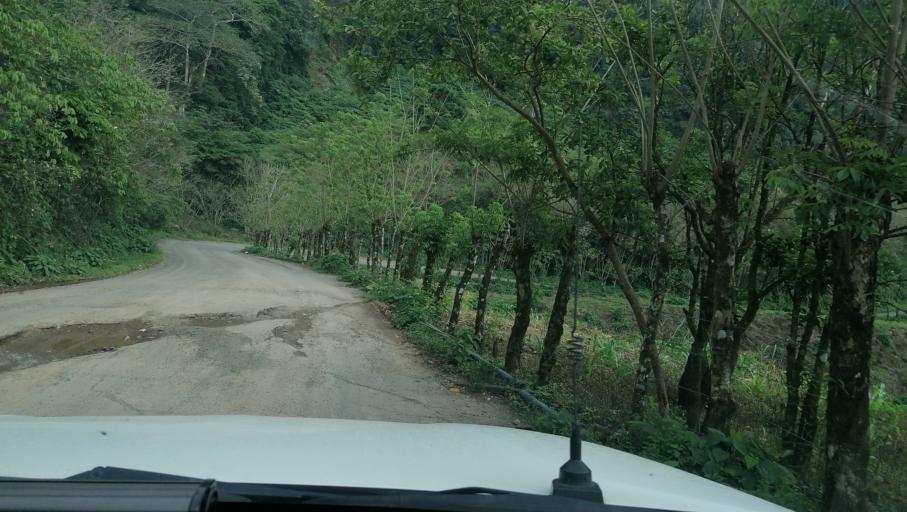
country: MX
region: Chiapas
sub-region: Francisco Leon
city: San Miguel la Sardina
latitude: 17.2412
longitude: -93.2991
